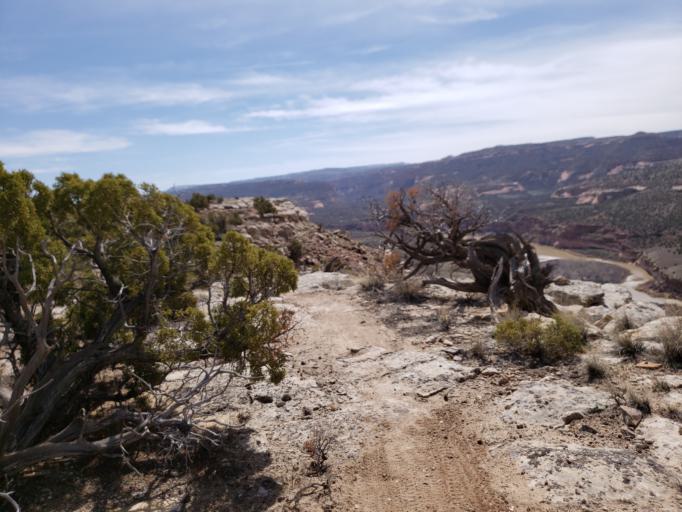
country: US
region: Colorado
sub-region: Mesa County
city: Loma
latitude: 39.1843
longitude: -108.8689
